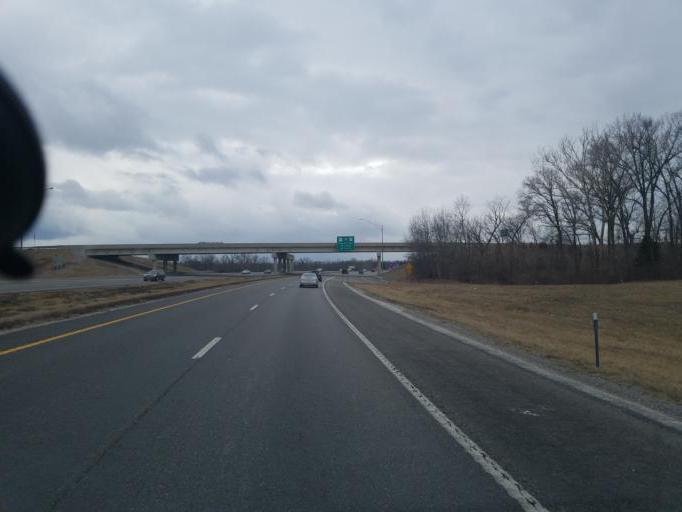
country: US
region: Missouri
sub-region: Boone County
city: Columbia
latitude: 38.9779
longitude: -92.2820
